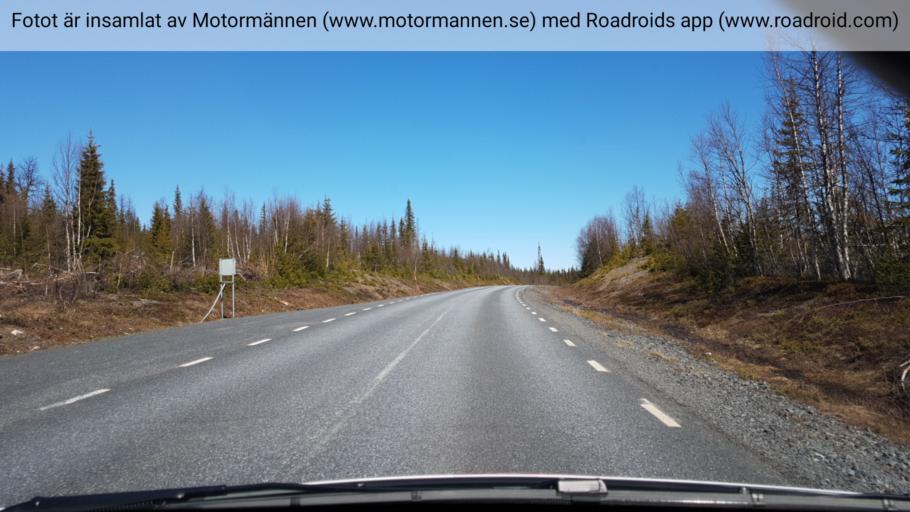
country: SE
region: Vaesterbotten
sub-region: Vilhelmina Kommun
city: Sjoberg
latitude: 64.9938
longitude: 15.8366
